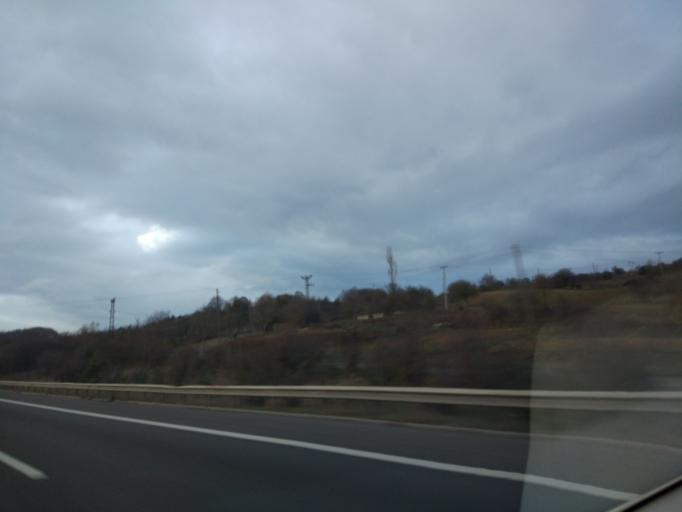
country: TR
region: Bolu
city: Bolu
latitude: 40.7228
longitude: 31.4971
